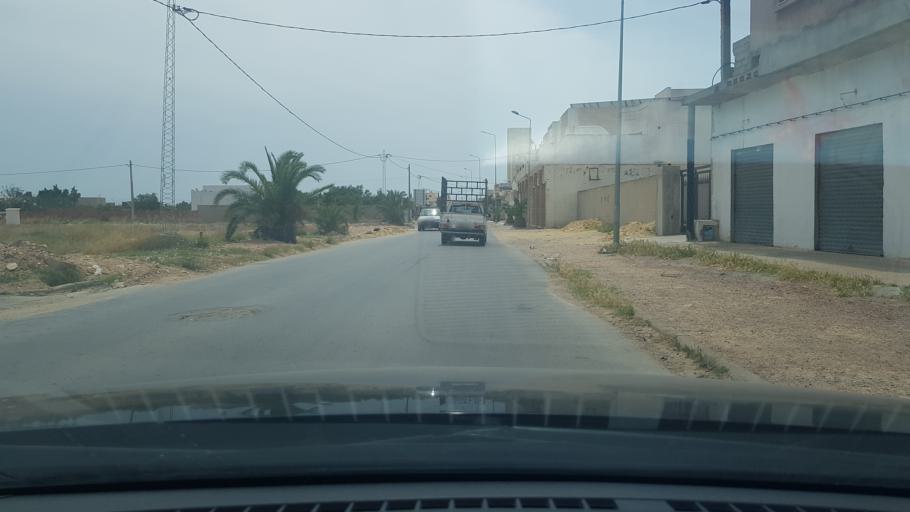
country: TN
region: Safaqis
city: Al Qarmadah
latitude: 34.8216
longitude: 10.7407
